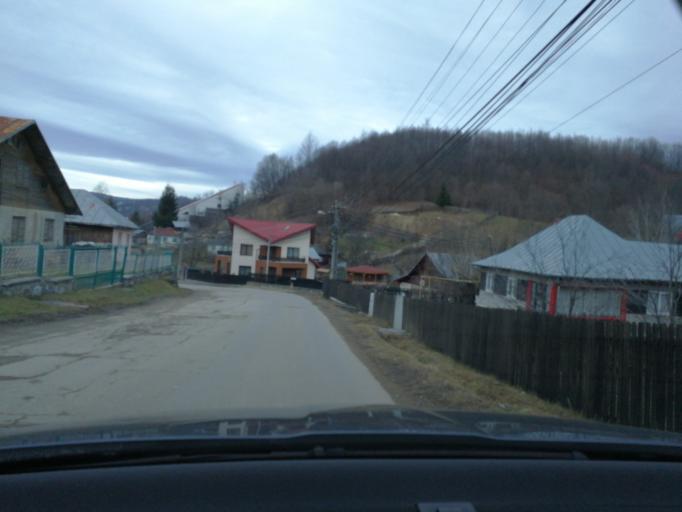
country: RO
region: Prahova
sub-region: Oras Breaza
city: Valea Tarsei
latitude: 45.1795
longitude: 25.6460
